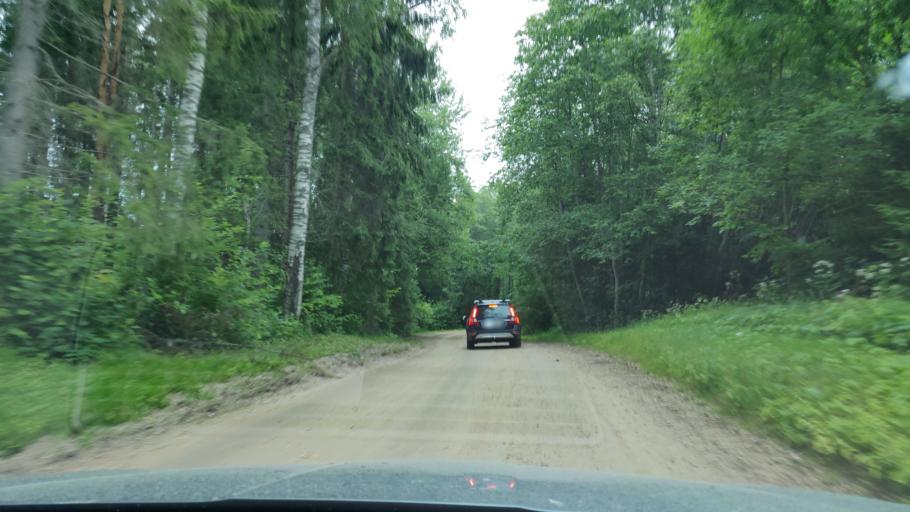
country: EE
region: Vorumaa
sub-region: Antsla vald
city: Vana-Antsla
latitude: 58.0334
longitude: 26.5519
